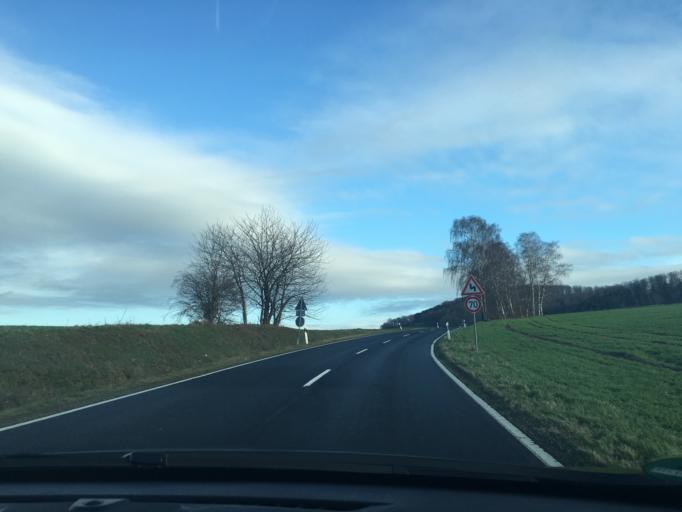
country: DE
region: Hesse
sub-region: Regierungsbezirk Kassel
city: Hofbieber
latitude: 50.5928
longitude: 9.8673
